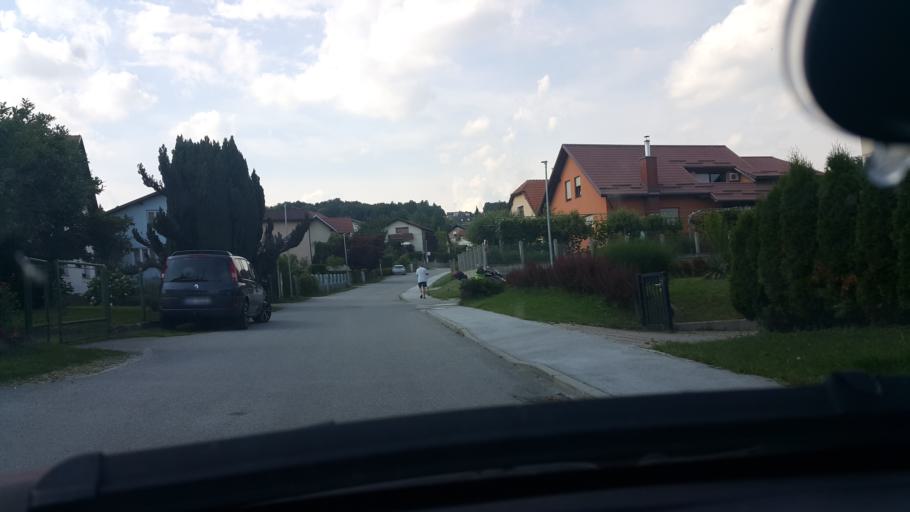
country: SI
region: Ptuj
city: Ptuj
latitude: 46.4285
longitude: 15.8824
